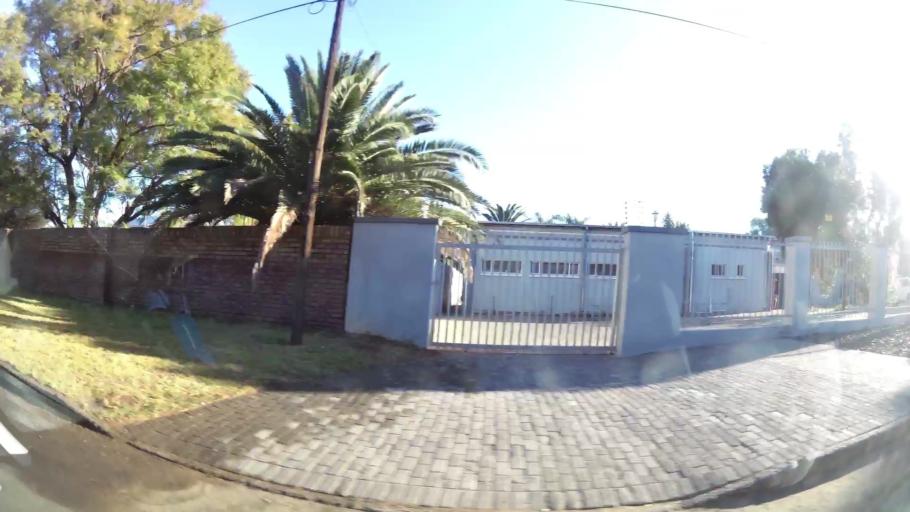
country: ZA
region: Northern Cape
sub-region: Frances Baard District Municipality
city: Kimberley
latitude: -28.7486
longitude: 24.7362
